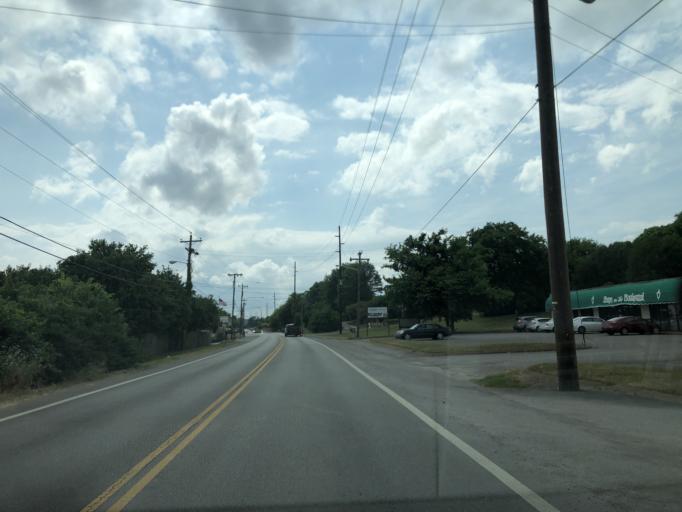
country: US
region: Tennessee
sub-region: Davidson County
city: Goodlettsville
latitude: 36.2634
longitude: -86.6947
